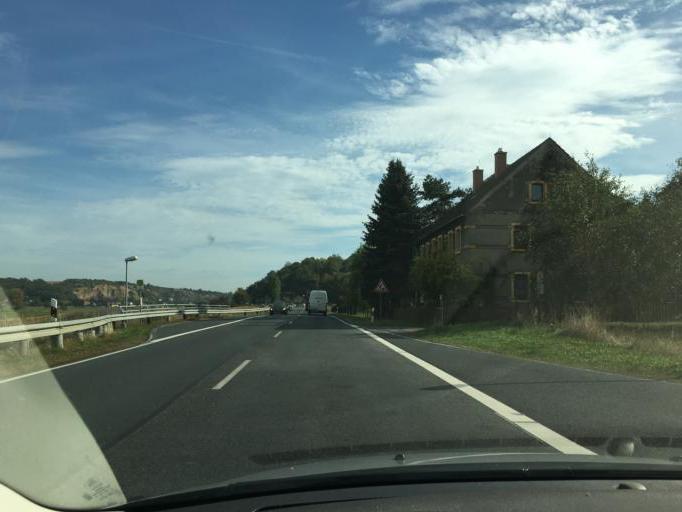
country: DE
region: Saxony
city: Meissen
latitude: 51.1901
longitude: 13.4228
